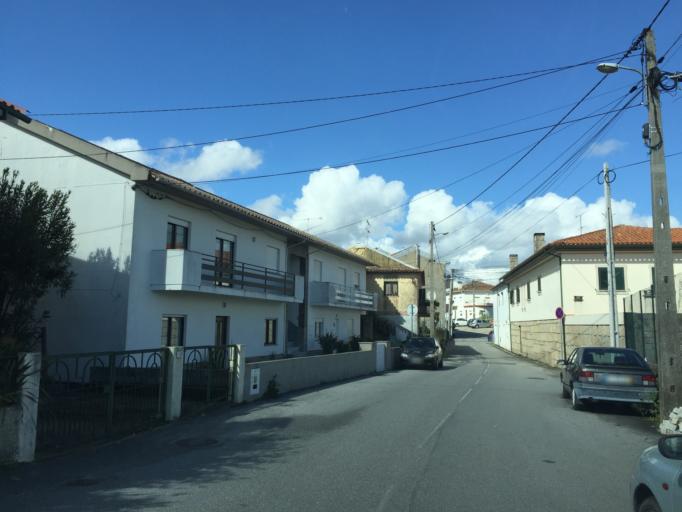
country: PT
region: Viseu
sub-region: Viseu
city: Abraveses
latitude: 40.6630
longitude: -7.9386
